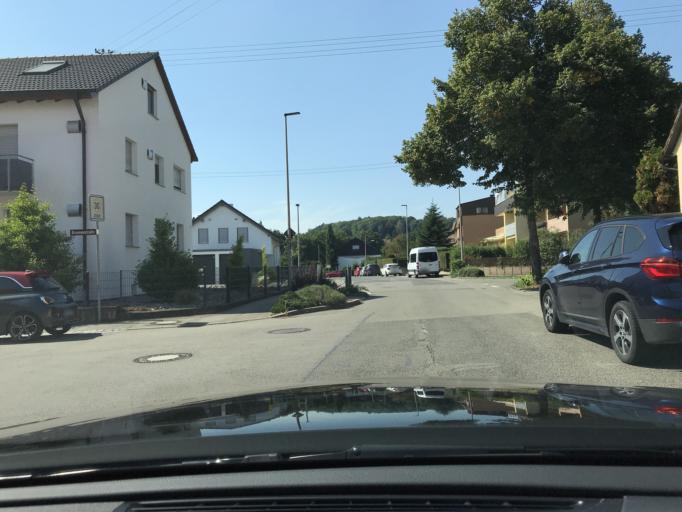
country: DE
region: Baden-Wuerttemberg
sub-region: Regierungsbezirk Stuttgart
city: Affalterbach
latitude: 48.9210
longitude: 9.3237
